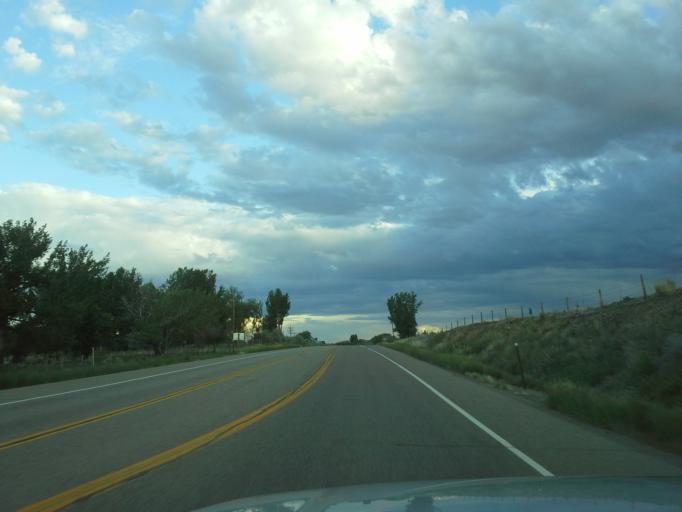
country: US
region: Wyoming
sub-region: Big Horn County
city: Basin
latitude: 44.3618
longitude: -108.0391
